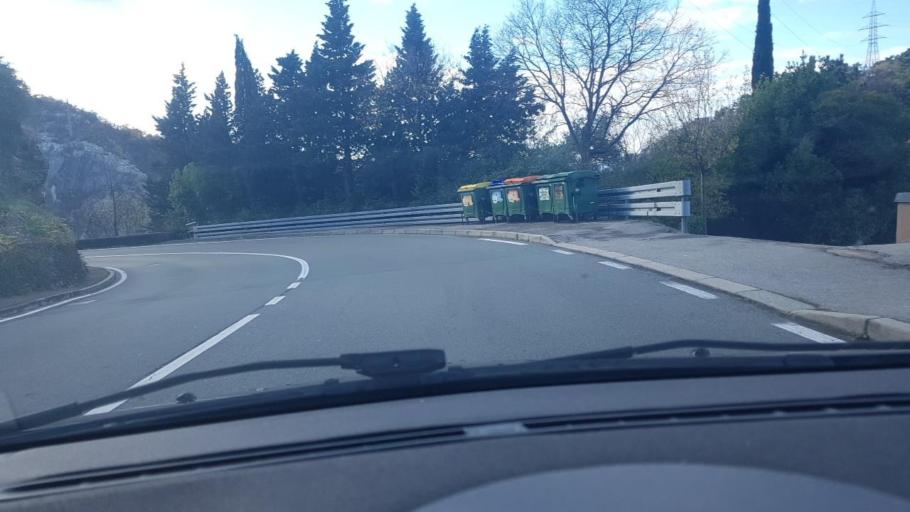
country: HR
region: Primorsko-Goranska
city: Cavle
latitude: 45.3400
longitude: 14.4649
